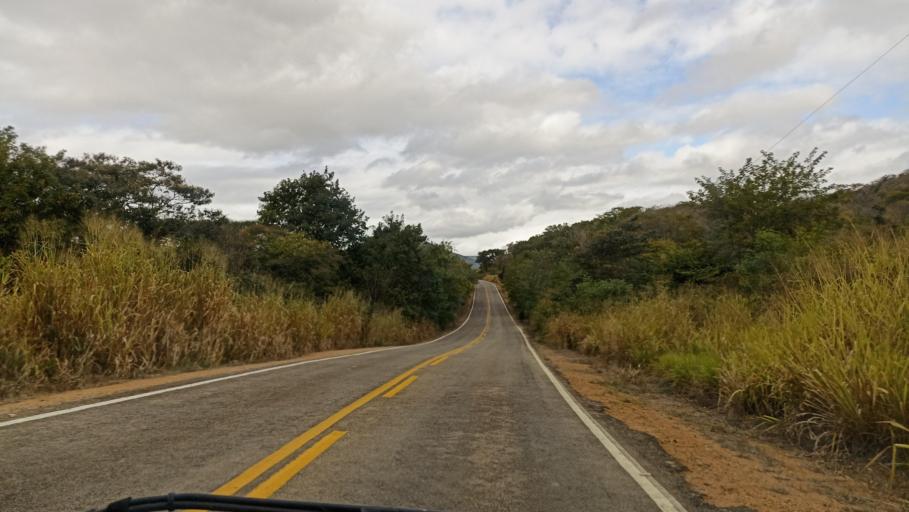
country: BR
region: Minas Gerais
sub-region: Joaima
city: Joaima
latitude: -16.6882
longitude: -40.9625
